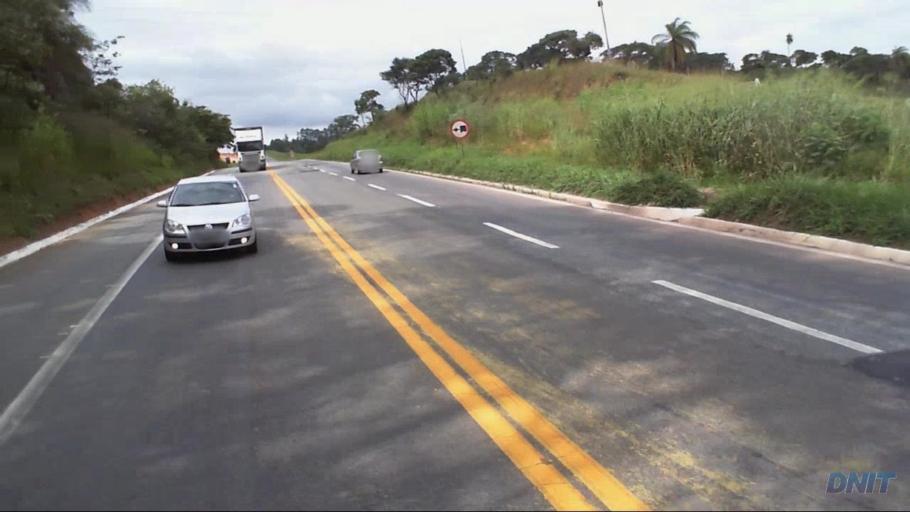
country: BR
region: Minas Gerais
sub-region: Caete
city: Caete
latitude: -19.7241
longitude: -43.5717
